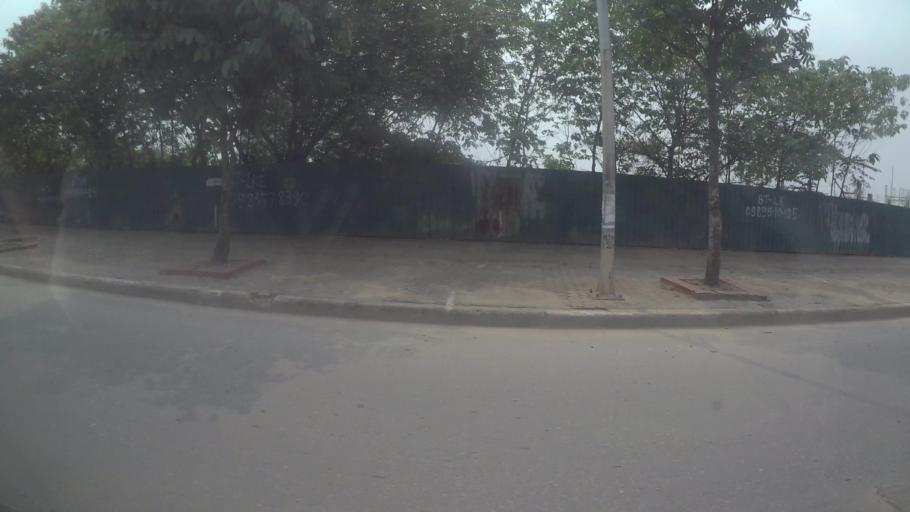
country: VN
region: Ha Noi
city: Thanh Xuan
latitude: 21.0076
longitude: 105.7735
